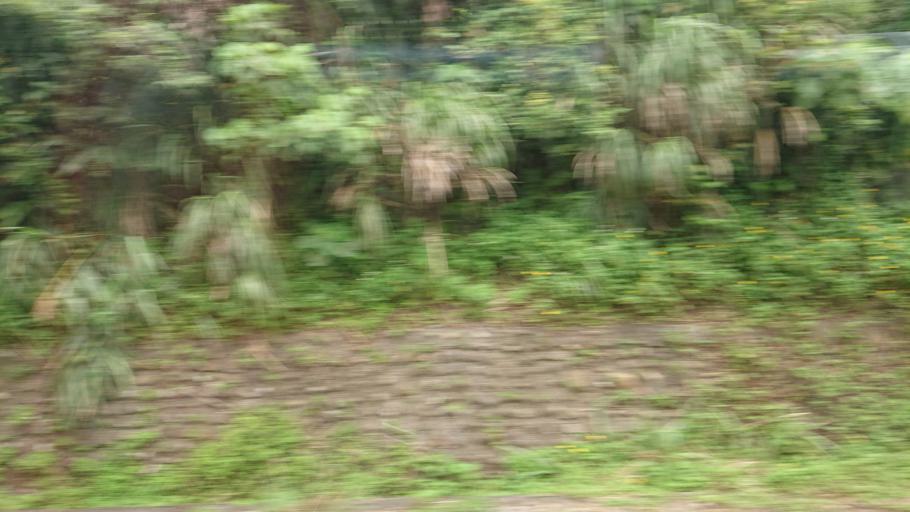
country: TW
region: Taiwan
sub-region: Keelung
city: Keelung
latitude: 24.9487
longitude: 121.9060
